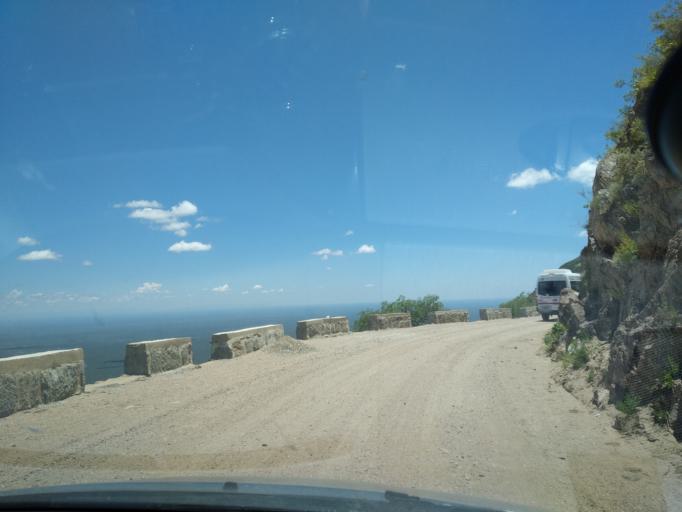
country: AR
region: Cordoba
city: Salsacate
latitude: -31.3762
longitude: -65.4079
